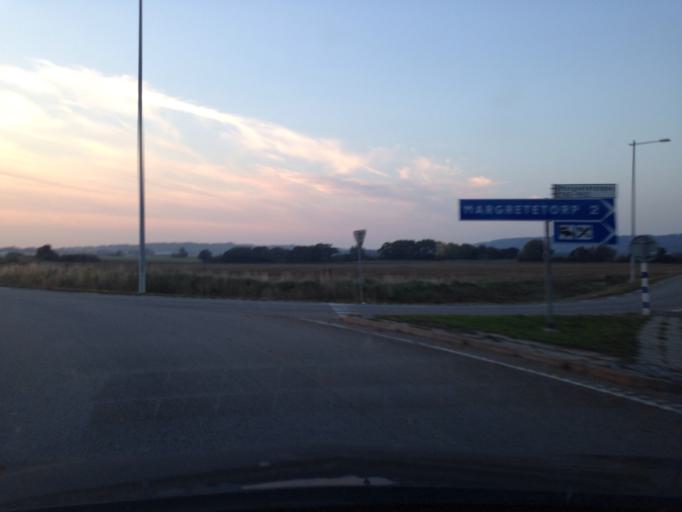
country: SE
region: Skane
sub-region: Bastads Kommun
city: Forslov
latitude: 56.3197
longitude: 12.8886
